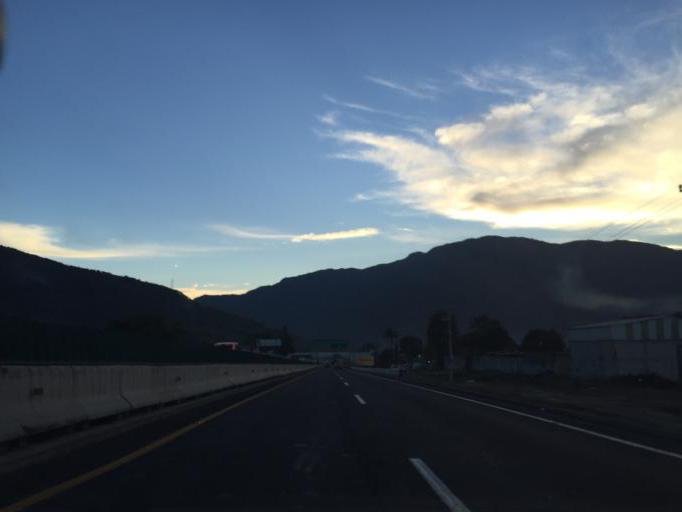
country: MX
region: Veracruz
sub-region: Nogales
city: Agricola Lazaro Cardenas
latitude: 18.8142
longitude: -97.1967
